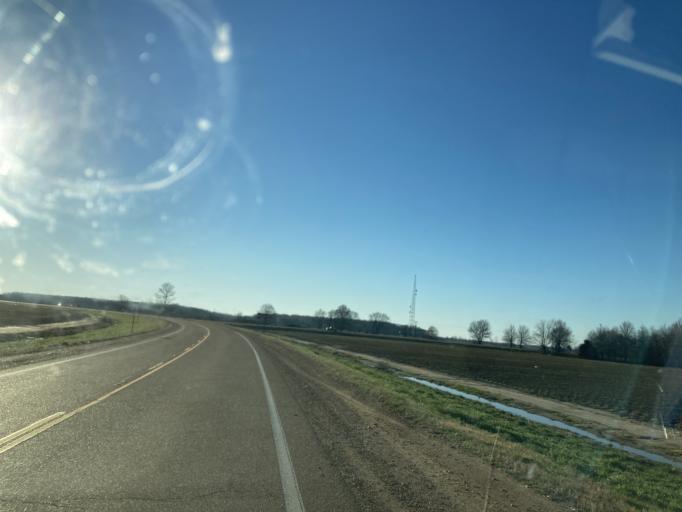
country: US
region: Mississippi
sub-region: Yazoo County
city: Yazoo City
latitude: 32.9309
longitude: -90.5863
